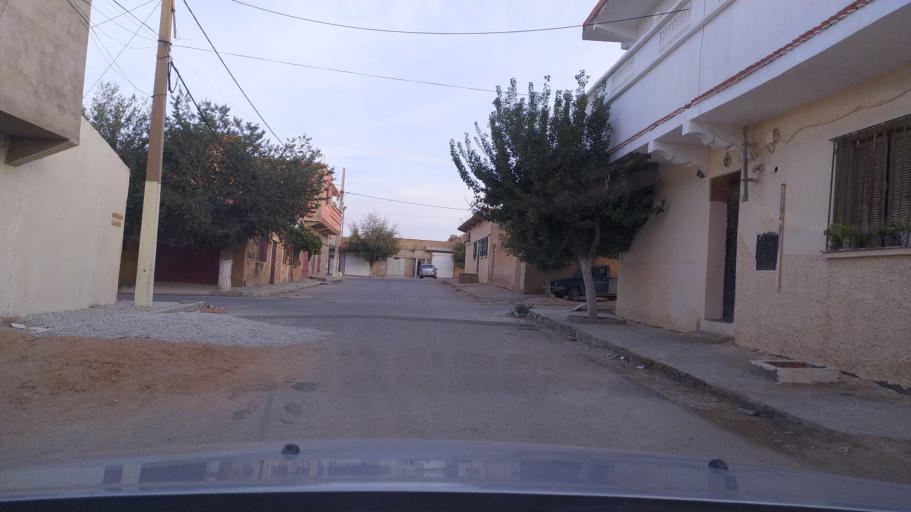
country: DZ
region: Tiaret
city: Frenda
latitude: 34.8991
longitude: 1.2364
